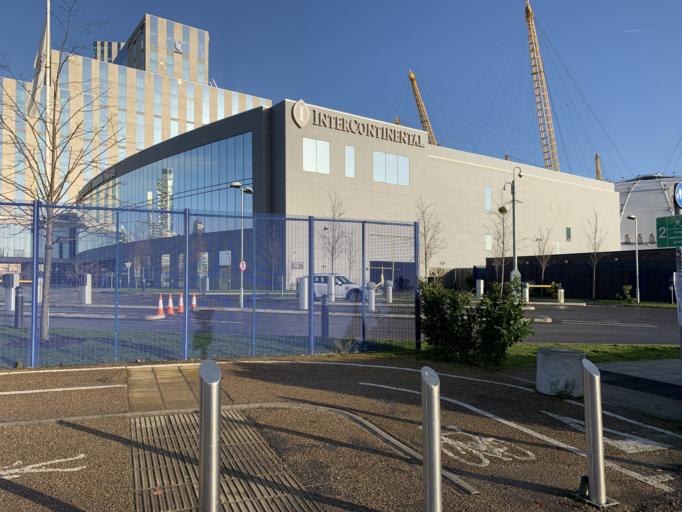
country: GB
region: England
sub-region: Greater London
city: Poplar
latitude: 51.5022
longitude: -0.0006
